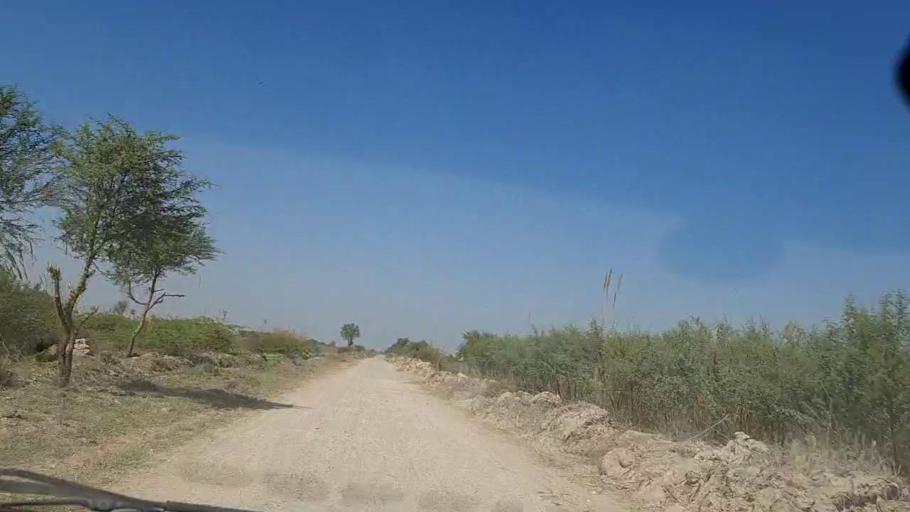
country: PK
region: Sindh
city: Mirwah Gorchani
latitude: 25.3835
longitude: 68.9720
